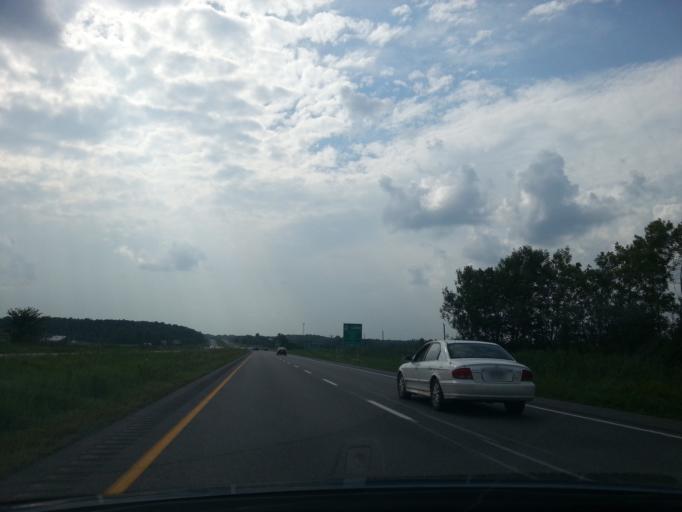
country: CA
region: Quebec
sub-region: Laurentides
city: Oka
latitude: 45.4246
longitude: -74.0930
